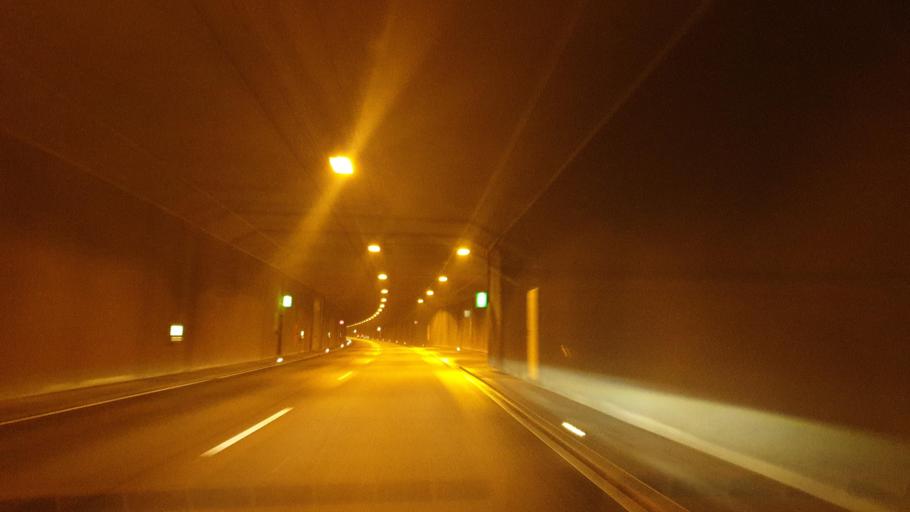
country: DE
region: North Rhine-Westphalia
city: Porta Westfalica
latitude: 52.2495
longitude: 8.9186
